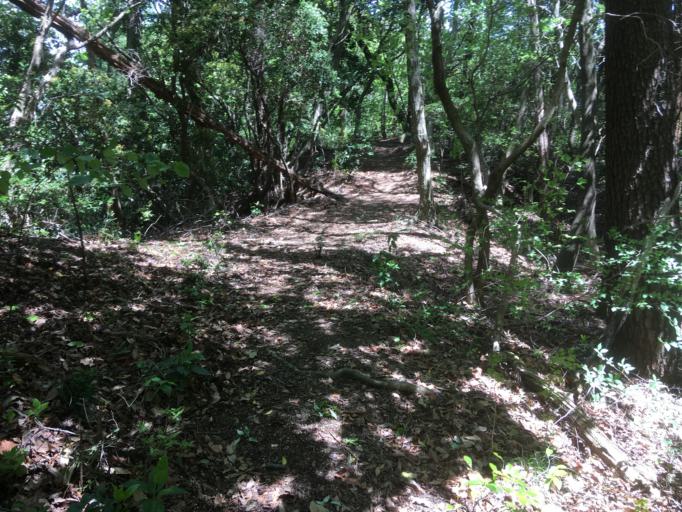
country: JP
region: Nara
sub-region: Ikoma-shi
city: Ikoma
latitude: 34.6921
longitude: 135.6876
